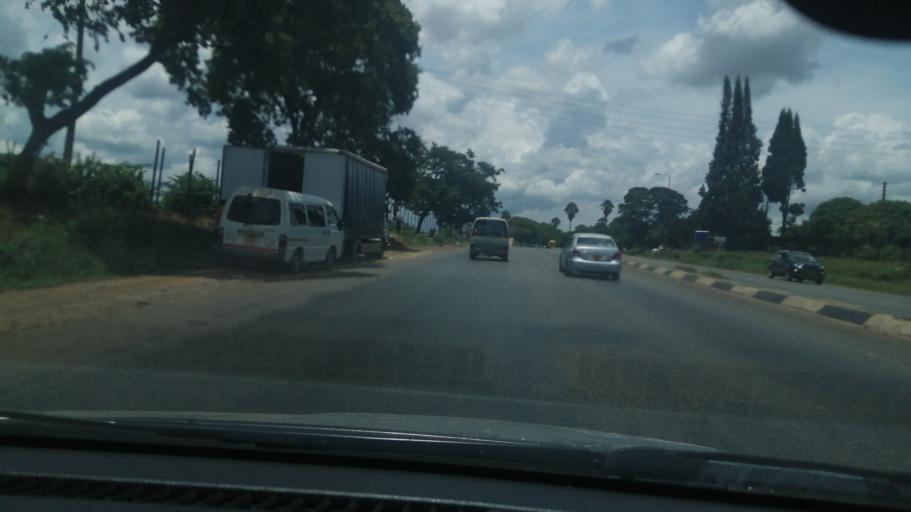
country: ZW
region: Harare
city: Harare
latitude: -17.8206
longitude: 30.9444
